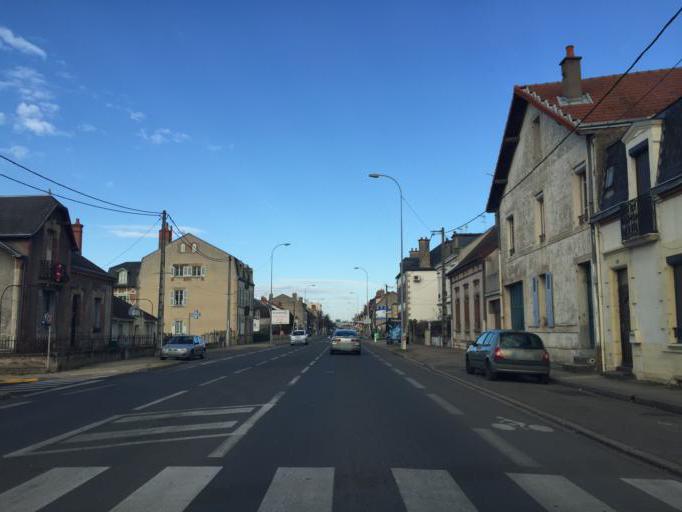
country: FR
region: Auvergne
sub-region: Departement de l'Allier
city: Moulins
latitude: 46.5550
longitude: 3.3361
